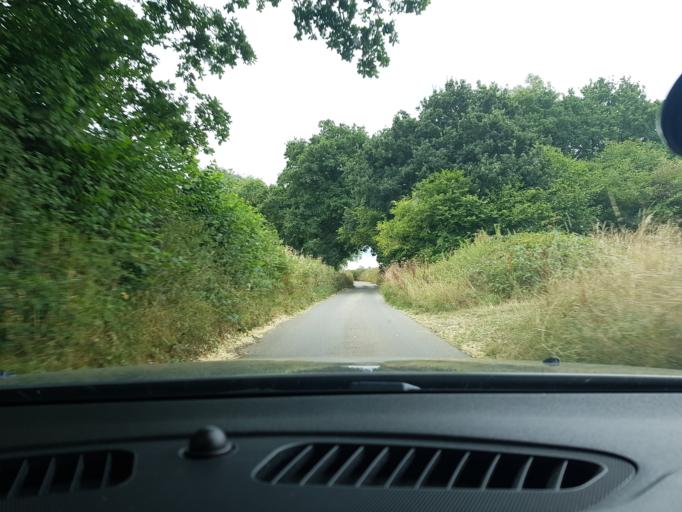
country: GB
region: England
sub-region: West Berkshire
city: Lambourn
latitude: 51.4761
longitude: -1.5058
